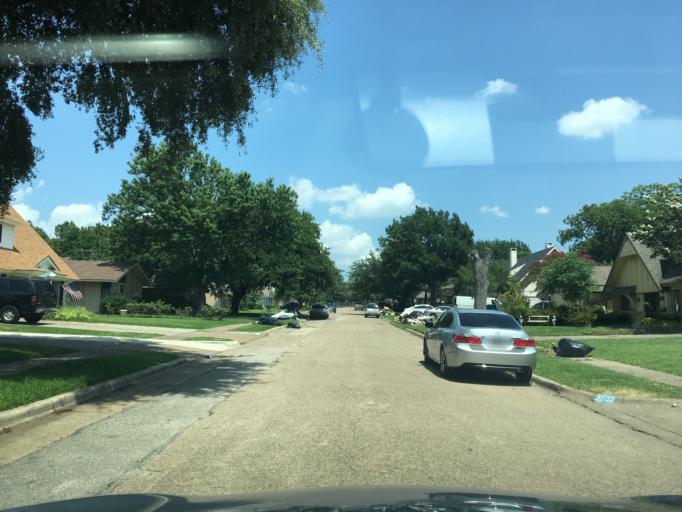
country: US
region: Texas
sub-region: Dallas County
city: Farmers Branch
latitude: 32.9148
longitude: -96.8588
